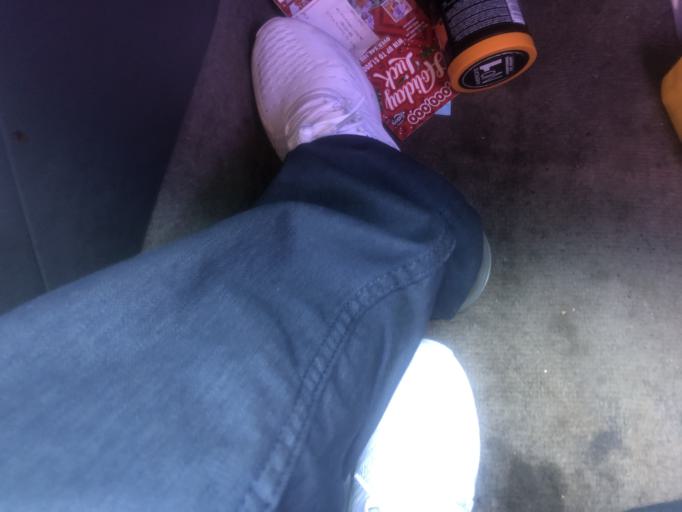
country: US
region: Florida
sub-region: Sumter County
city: Lake Panasoffkee
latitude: 28.7928
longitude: -82.0880
